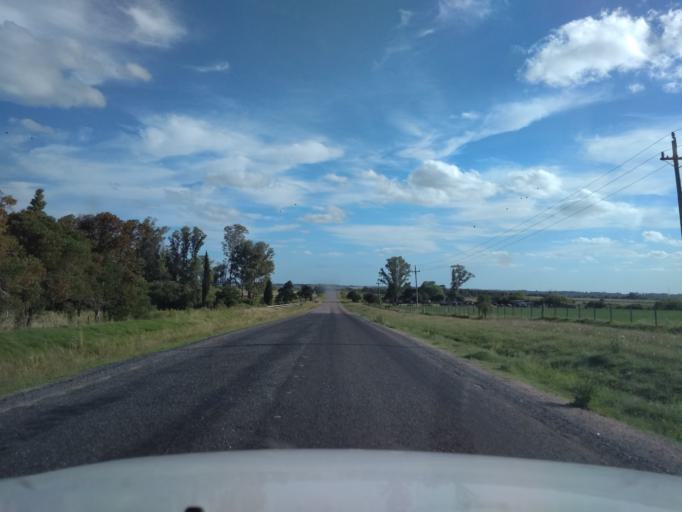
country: UY
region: Canelones
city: San Ramon
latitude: -34.2520
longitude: -55.9262
